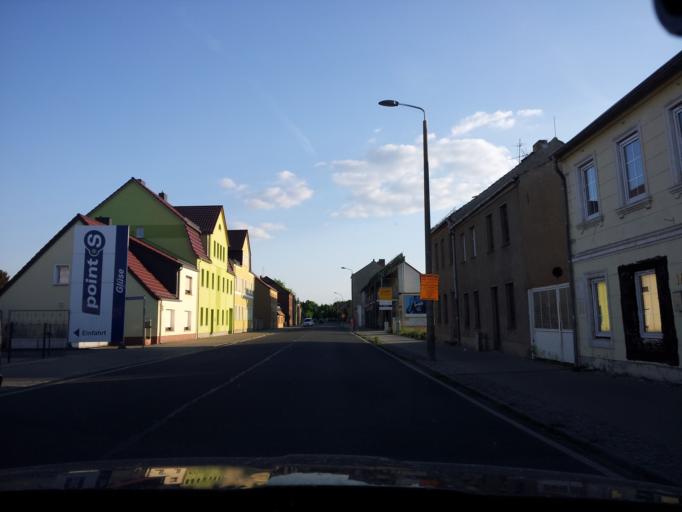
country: DE
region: Brandenburg
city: Luckenwalde
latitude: 52.0822
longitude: 13.1619
